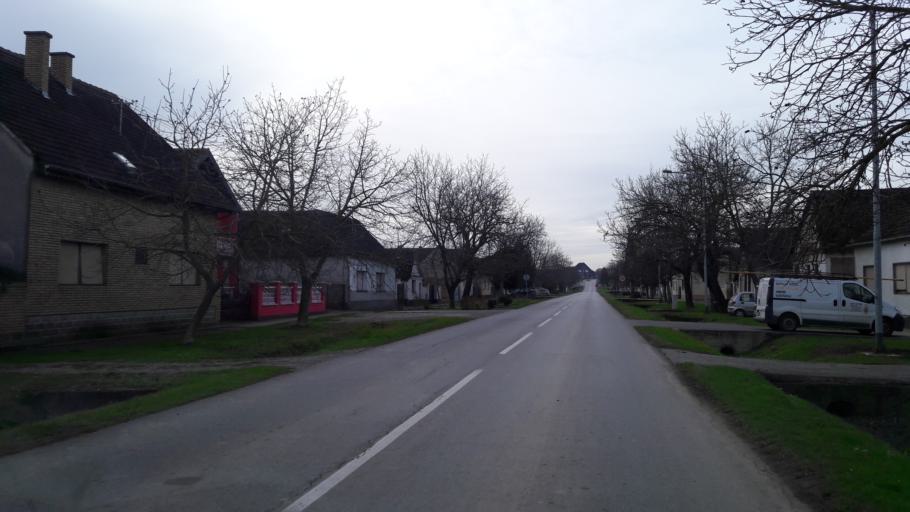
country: HR
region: Osjecko-Baranjska
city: Semeljci
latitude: 45.3643
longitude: 18.5452
